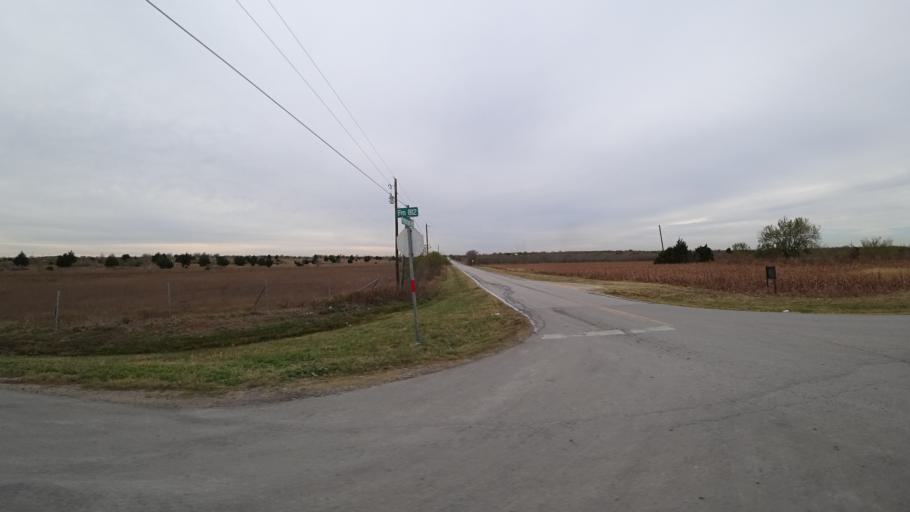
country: US
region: Texas
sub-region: Travis County
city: Garfield
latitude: 30.1102
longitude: -97.6230
